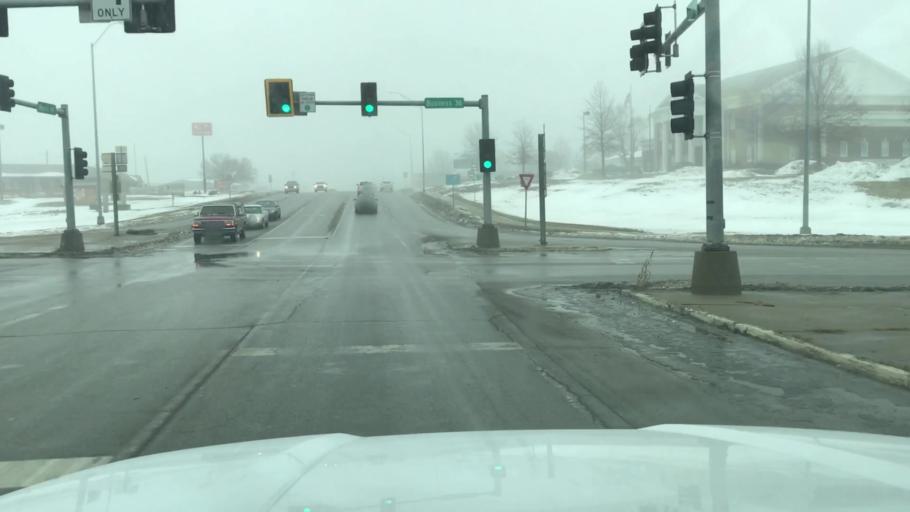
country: US
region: Missouri
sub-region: Clinton County
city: Cameron
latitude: 39.7484
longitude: -94.2351
